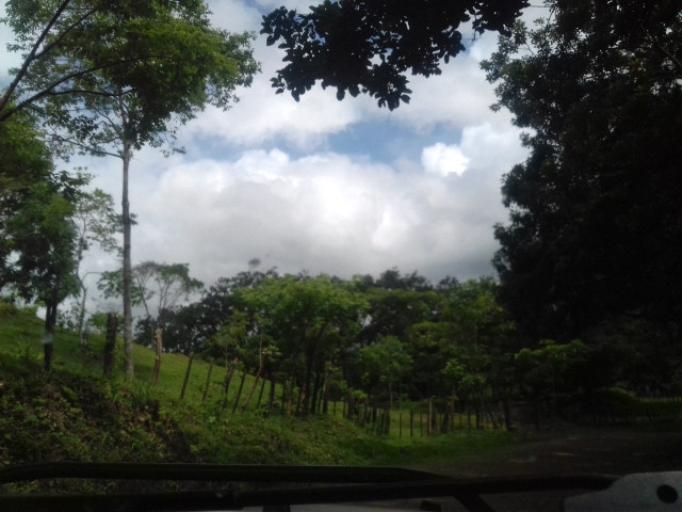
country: NI
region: Matagalpa
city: Matiguas
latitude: 12.8596
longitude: -85.3912
